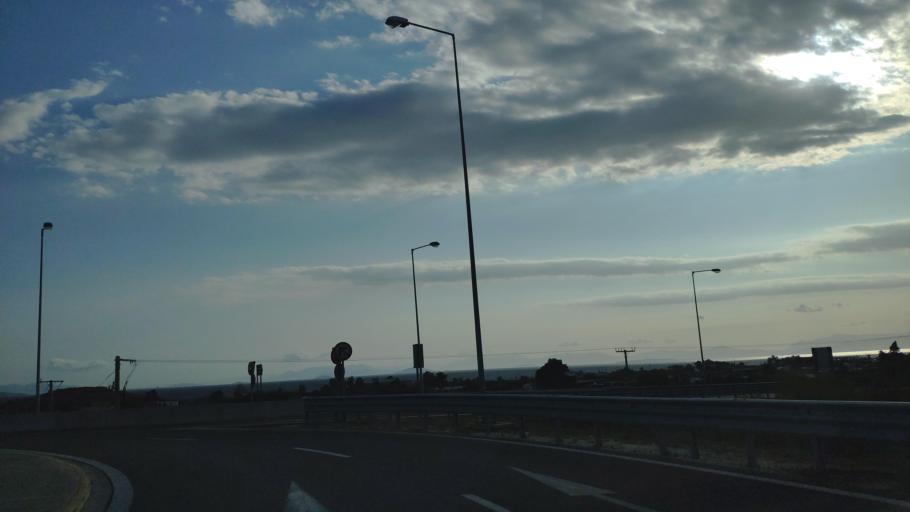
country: GR
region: Attica
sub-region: Nomarchia Dytikis Attikis
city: Megara
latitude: 37.9855
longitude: 23.3514
